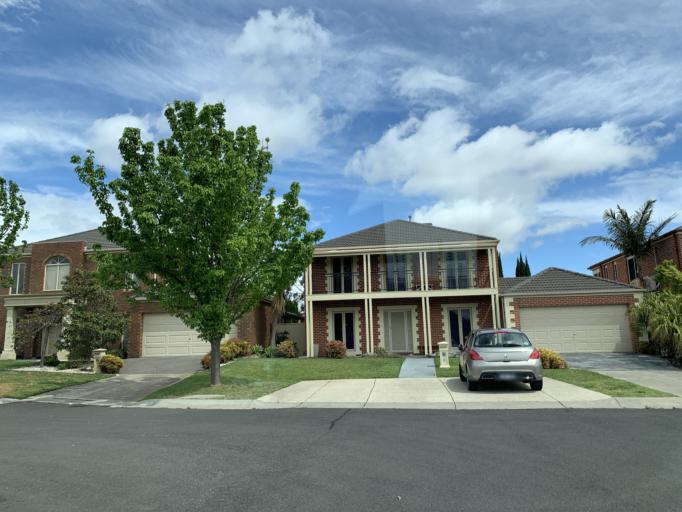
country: AU
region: Victoria
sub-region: Brimbank
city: Cairnlea
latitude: -37.7612
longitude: 144.7943
